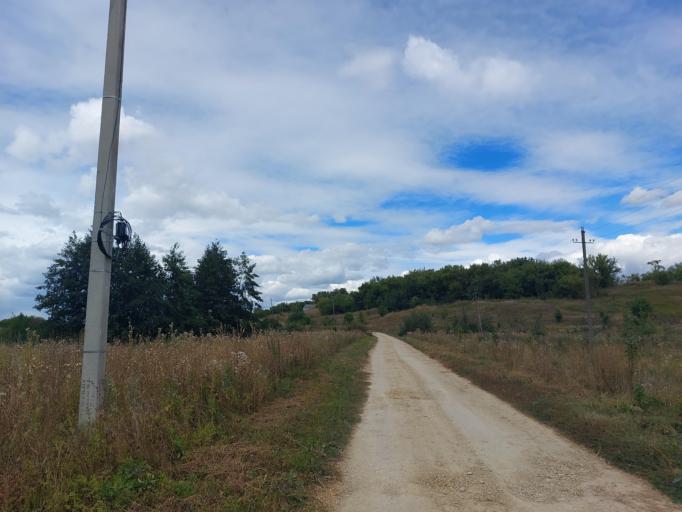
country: RU
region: Lipetsk
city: Terbuny
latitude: 52.2684
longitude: 38.2046
